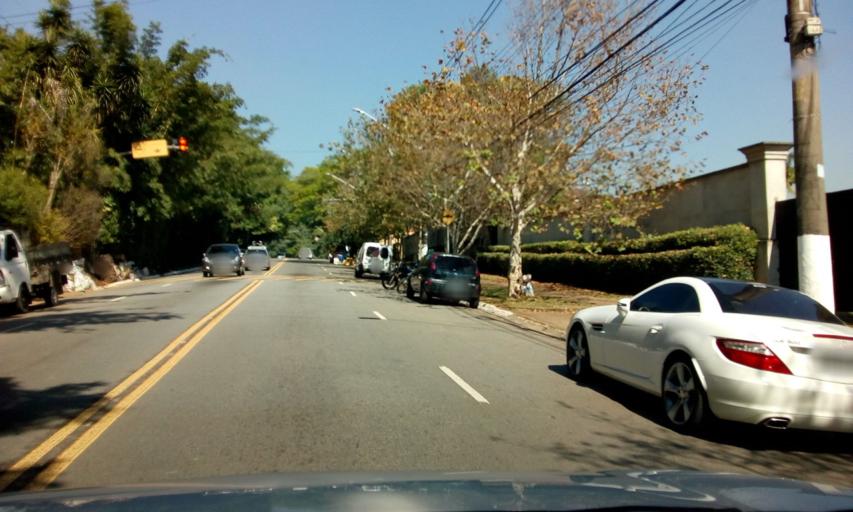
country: BR
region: Sao Paulo
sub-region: Sao Paulo
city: Sao Paulo
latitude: -23.5916
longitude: -46.7058
